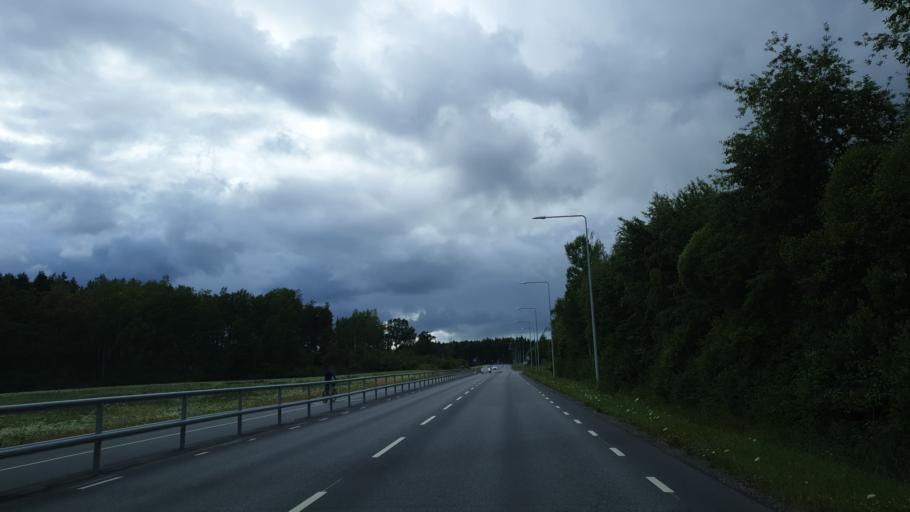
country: SE
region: Stockholm
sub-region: Jarfalla Kommun
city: Jakobsberg
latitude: 59.4216
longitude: 17.8091
